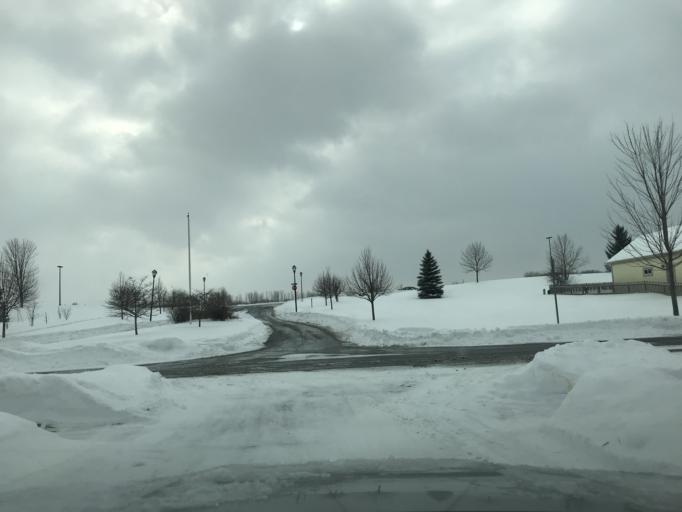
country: US
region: Wisconsin
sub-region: Dane County
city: Sun Prairie
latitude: 43.1659
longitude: -89.2825
